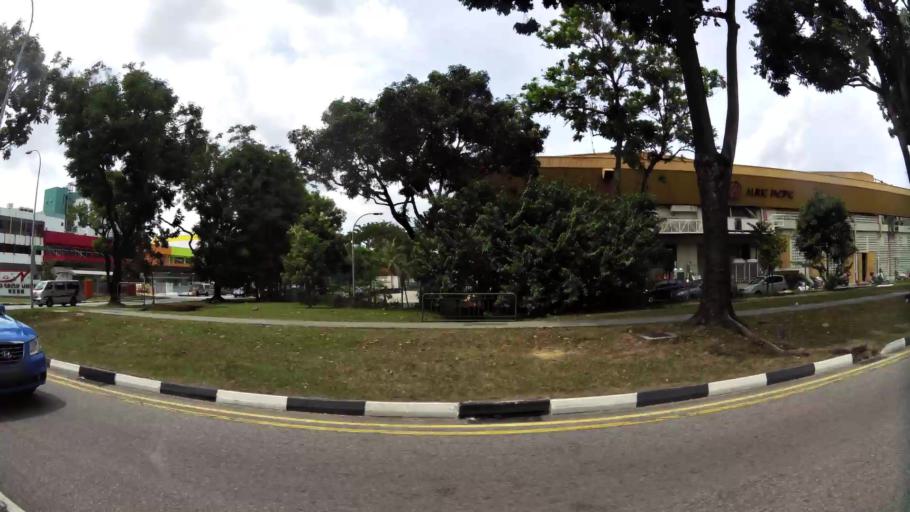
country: MY
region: Johor
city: Johor Bahru
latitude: 1.3331
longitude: 103.7085
